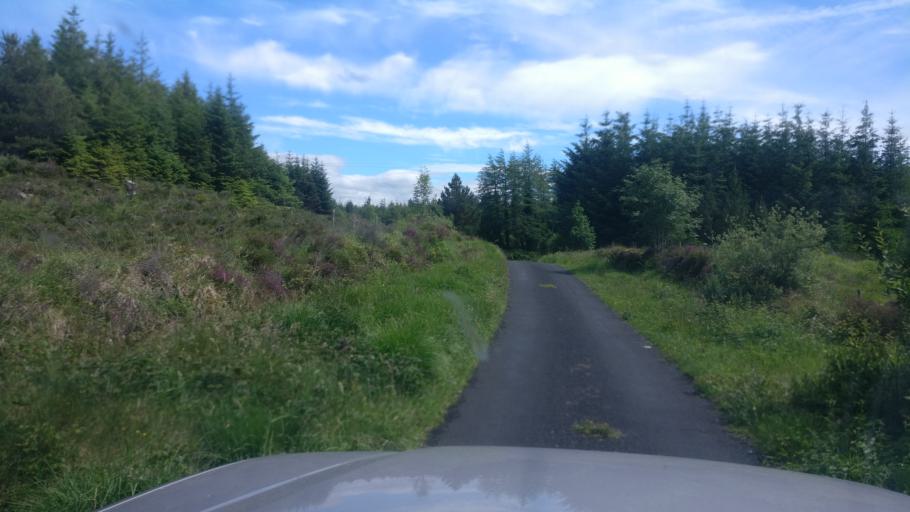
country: IE
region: Connaught
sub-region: County Galway
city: Gort
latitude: 53.0648
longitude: -8.6987
